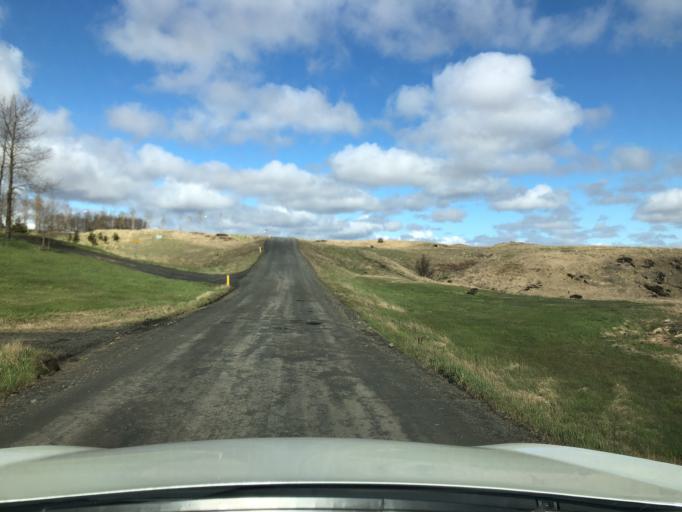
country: IS
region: South
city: Selfoss
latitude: 63.9250
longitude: -20.6782
